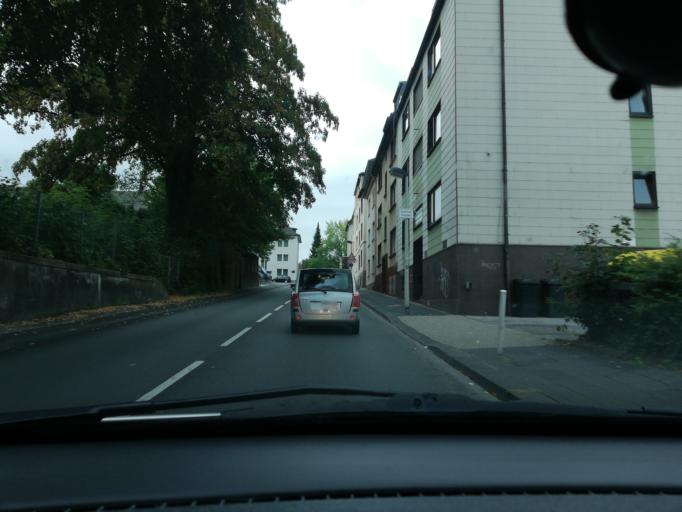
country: DE
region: North Rhine-Westphalia
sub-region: Regierungsbezirk Dusseldorf
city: Solingen
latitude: 51.1715
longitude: 7.0916
